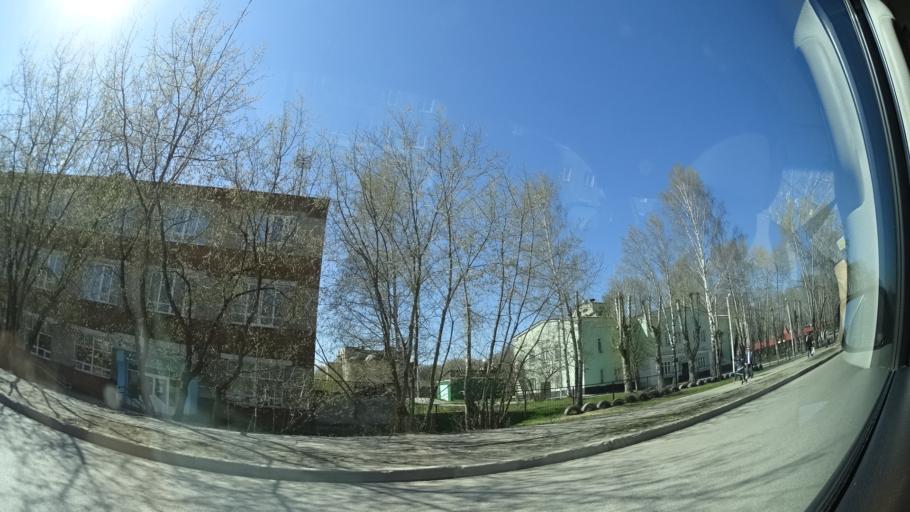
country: RU
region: Perm
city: Perm
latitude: 58.1111
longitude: 56.3039
